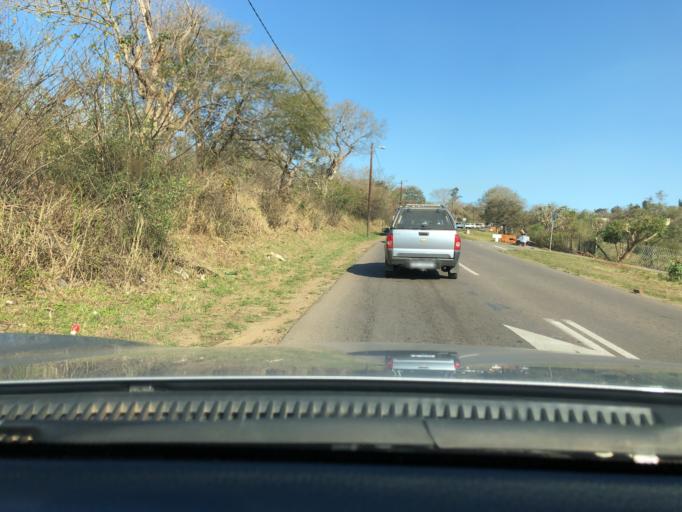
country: ZA
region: KwaZulu-Natal
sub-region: uMgungundlovu District Municipality
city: Pietermaritzburg
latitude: -29.6635
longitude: 30.4450
